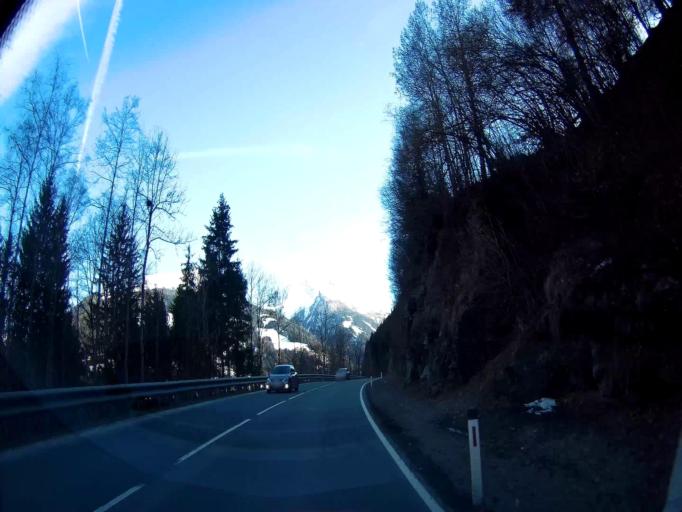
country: AT
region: Salzburg
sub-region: Politischer Bezirk Sankt Johann im Pongau
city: Bad Gastein
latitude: 47.1329
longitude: 13.1287
